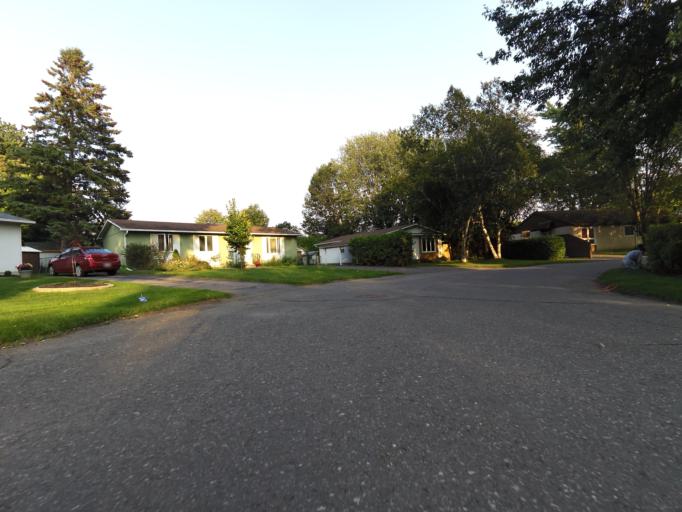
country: CA
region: Ontario
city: Bells Corners
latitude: 45.2888
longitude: -75.8816
